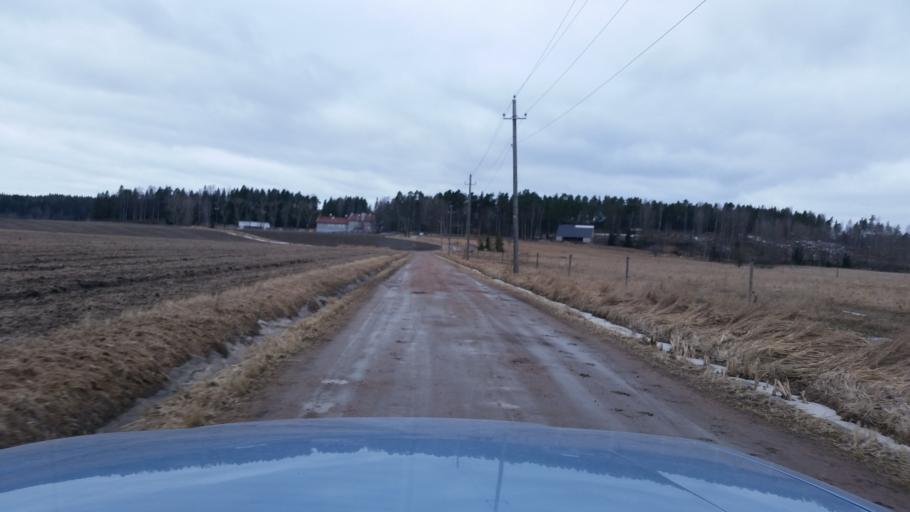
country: FI
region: Uusimaa
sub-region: Helsinki
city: Kauniainen
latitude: 60.2819
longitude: 24.6856
